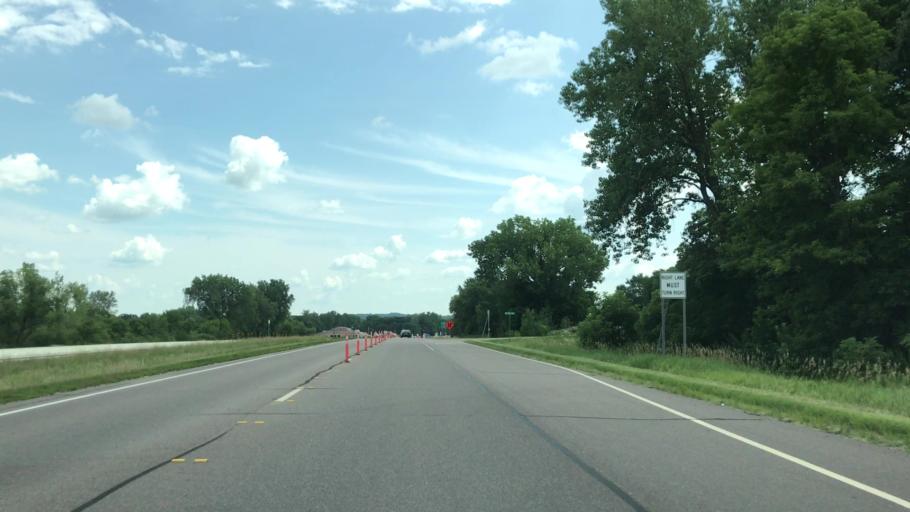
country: US
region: Minnesota
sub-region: Nicollet County
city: Saint Peter
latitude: 44.3548
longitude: -93.9551
